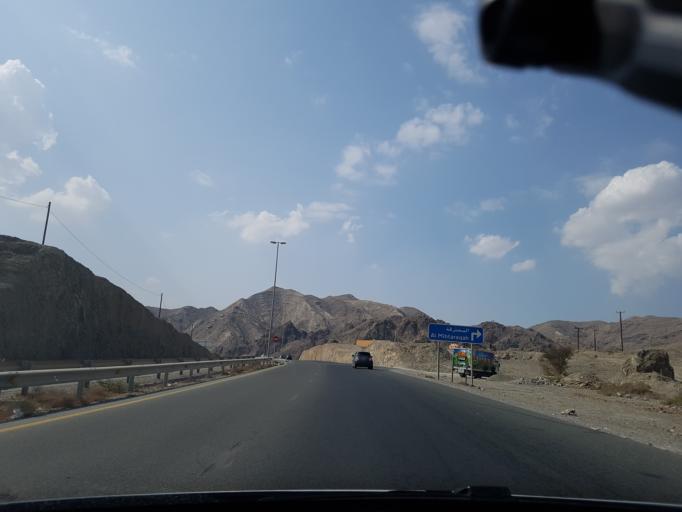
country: AE
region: Al Fujayrah
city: Dibba Al-Fujairah
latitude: 25.5325
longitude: 56.1348
